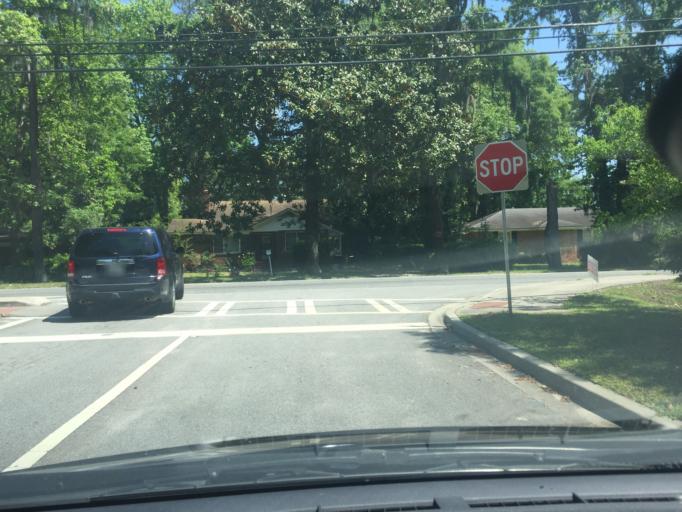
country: US
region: Georgia
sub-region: Chatham County
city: Savannah
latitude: 32.0261
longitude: -81.1148
